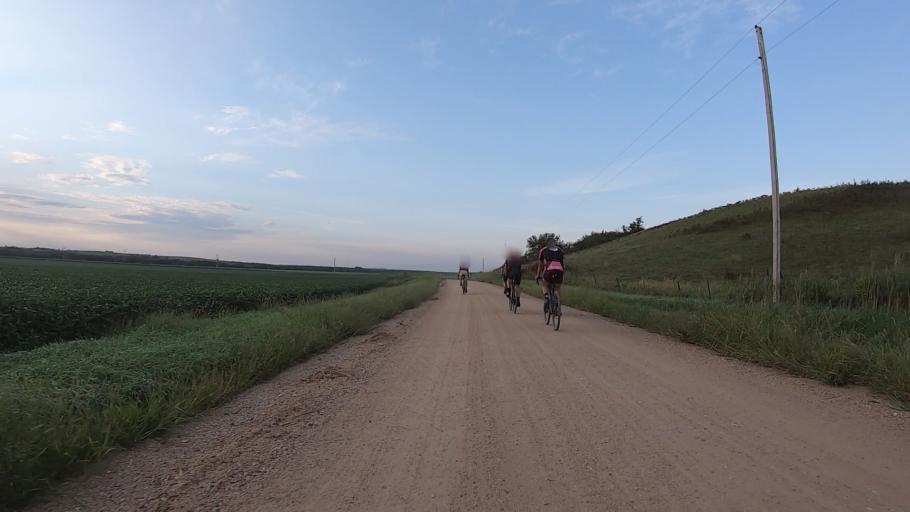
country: US
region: Kansas
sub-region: Marshall County
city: Marysville
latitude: 39.8265
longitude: -96.6658
